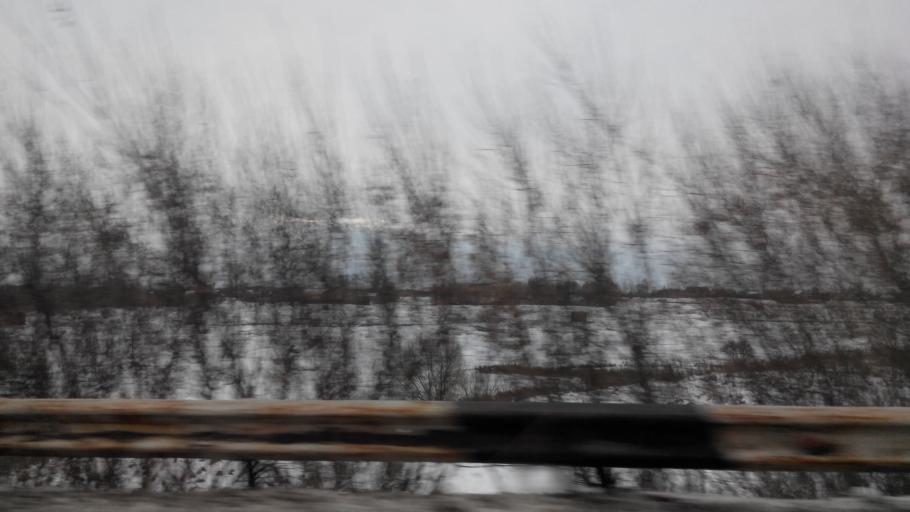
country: RU
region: Tula
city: Mayskiy
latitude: 53.9808
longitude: 38.2240
